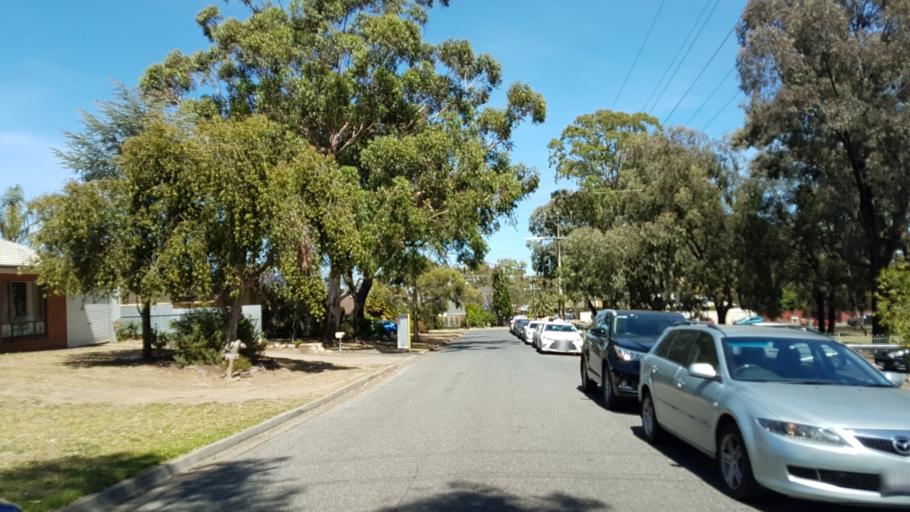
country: AU
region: South Australia
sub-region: Tea Tree Gully
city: Hope Valley
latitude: -34.8228
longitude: 138.7163
